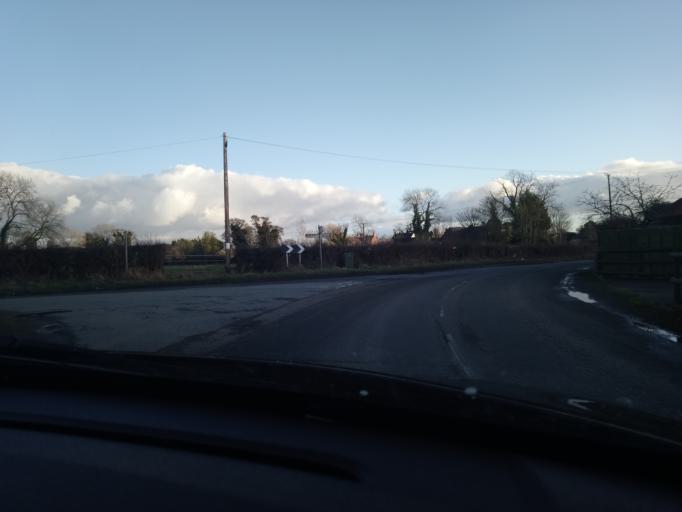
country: GB
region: England
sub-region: Shropshire
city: Petton
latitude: 52.8965
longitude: -2.8010
